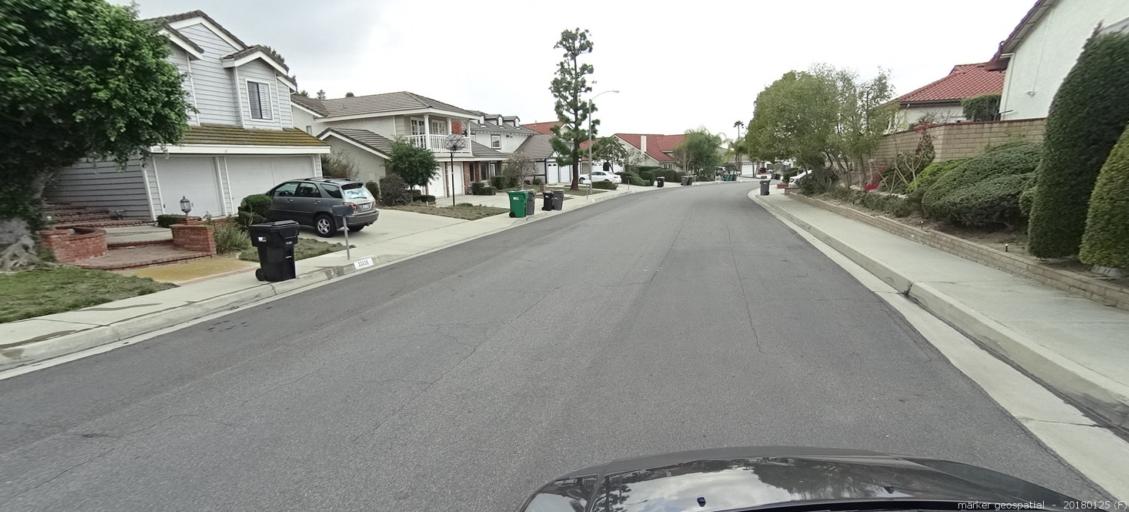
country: US
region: California
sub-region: Los Angeles County
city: Diamond Bar
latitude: 33.9948
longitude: -117.8306
